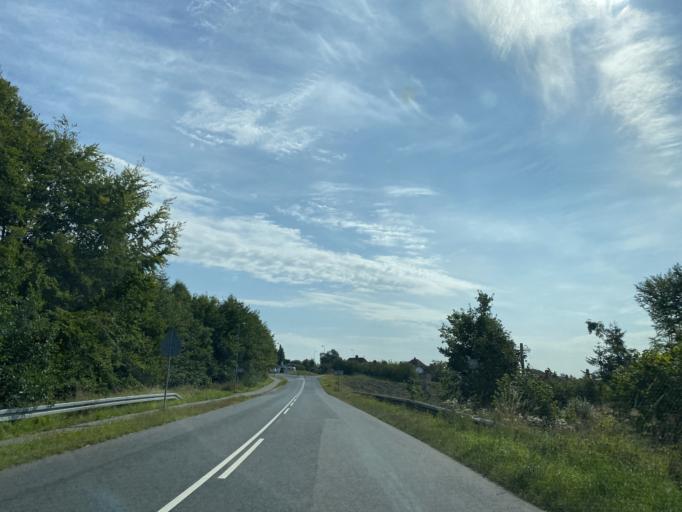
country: DK
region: Central Jutland
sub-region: Favrskov Kommune
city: Hammel
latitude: 56.2618
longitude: 9.8493
